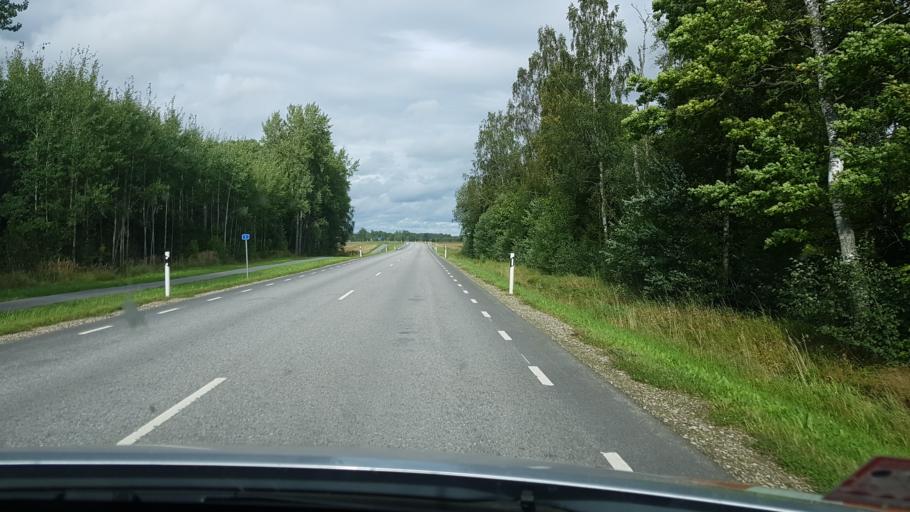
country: EE
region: Viljandimaa
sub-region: Moisakuela linn
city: Moisakula
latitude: 58.1067
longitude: 25.1895
